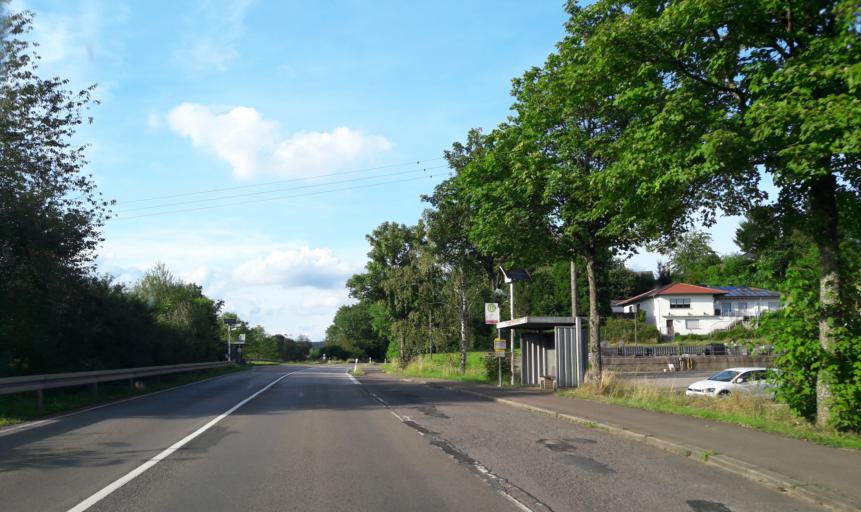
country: DE
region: Saarland
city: Marpingen
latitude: 49.4649
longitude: 7.0655
